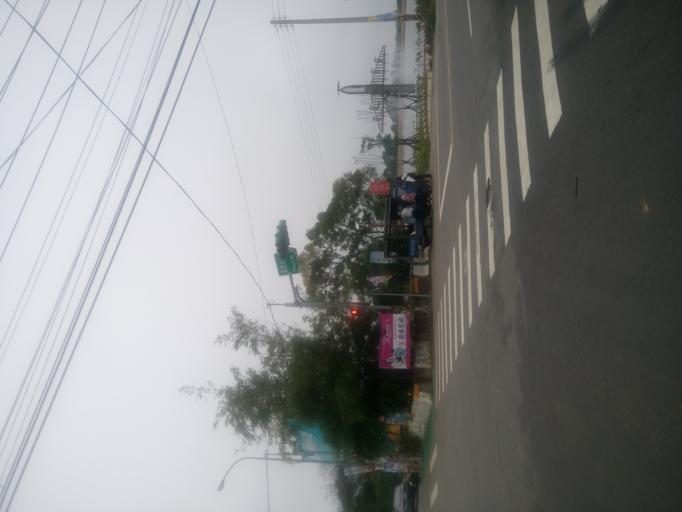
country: TW
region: Taiwan
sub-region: Hsinchu
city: Zhubei
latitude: 24.9390
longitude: 121.0857
